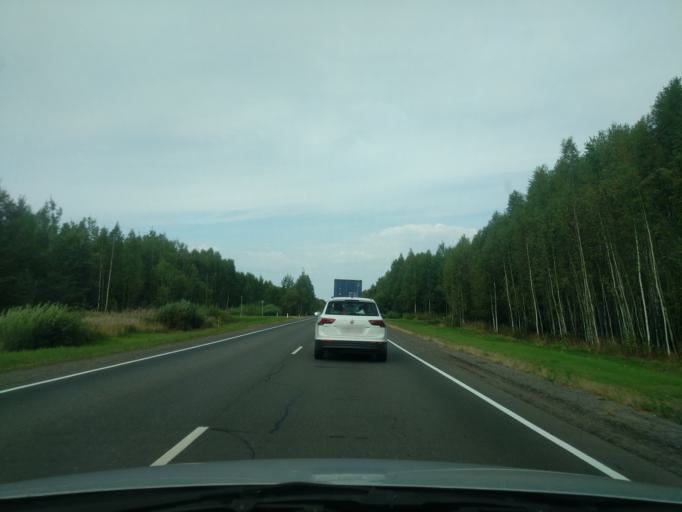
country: RU
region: Kirov
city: Leninskoye
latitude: 58.2851
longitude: 47.2490
